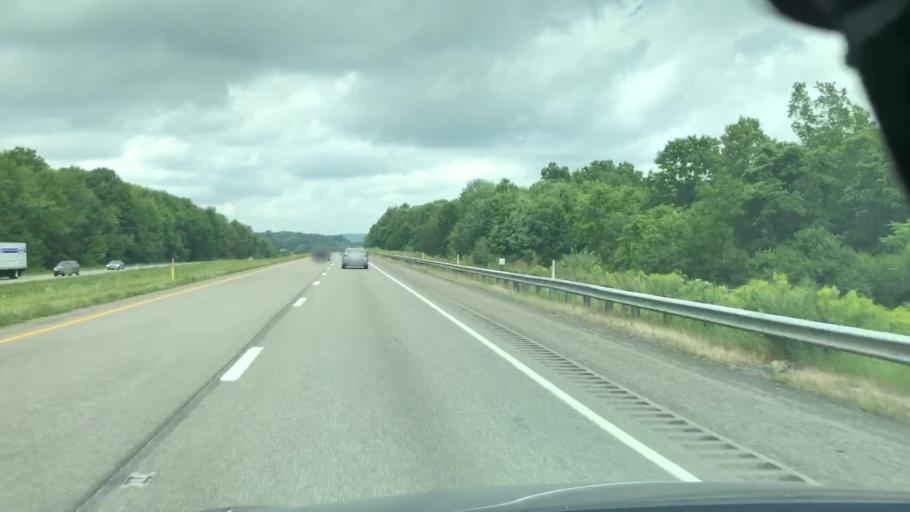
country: US
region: Pennsylvania
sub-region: Crawford County
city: Meadville
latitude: 41.5782
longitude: -80.1788
